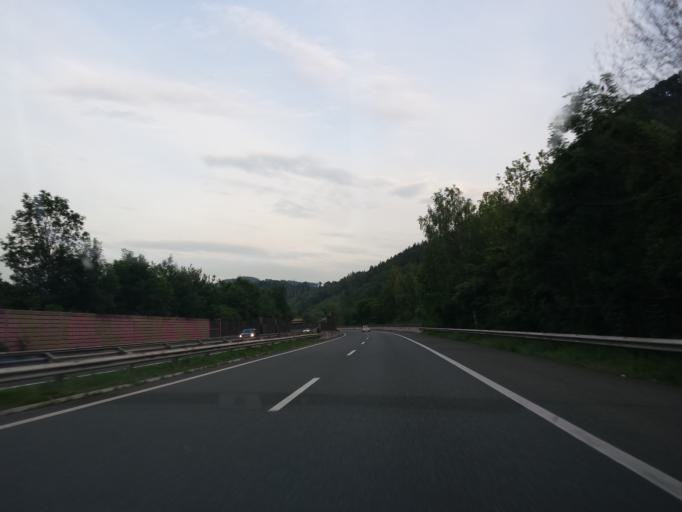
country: AT
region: Styria
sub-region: Politischer Bezirk Graz-Umgebung
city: Deutschfeistritz
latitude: 47.2101
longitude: 15.3099
